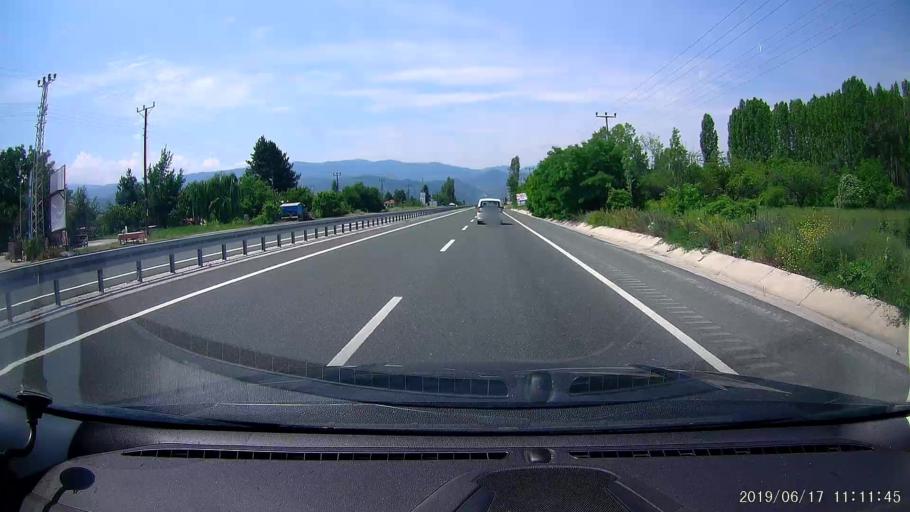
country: TR
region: Kastamonu
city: Tosya
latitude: 40.9822
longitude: 34.0052
